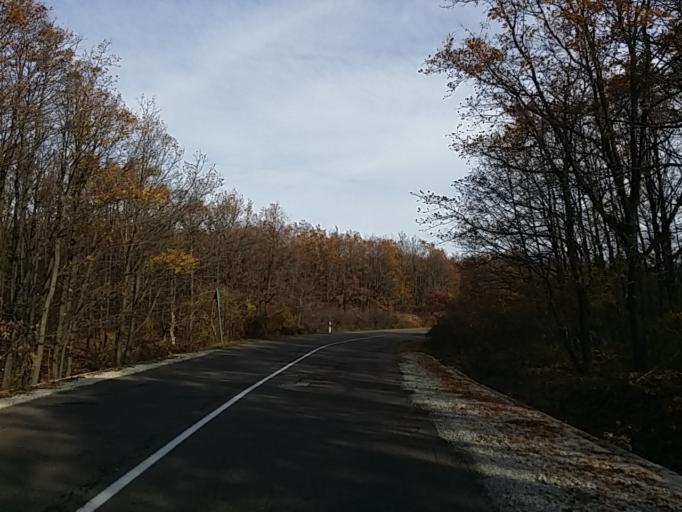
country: HU
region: Heves
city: Gyongyossolymos
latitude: 47.8470
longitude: 19.9594
